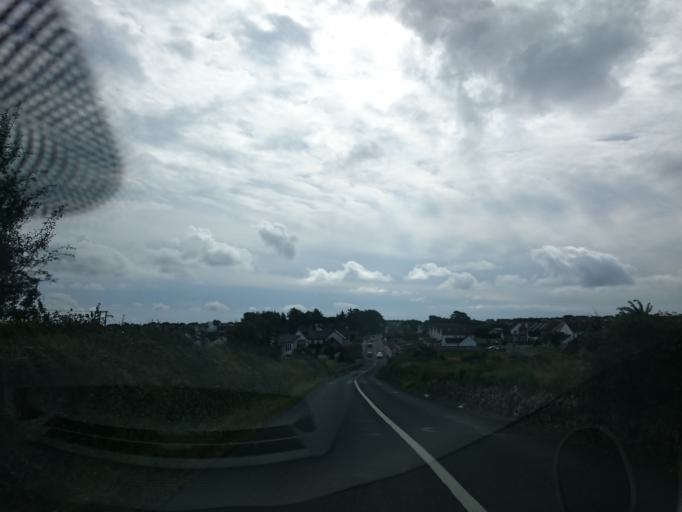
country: IE
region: Munster
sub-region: Waterford
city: Tra Mhor
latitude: 52.1744
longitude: -7.1588
